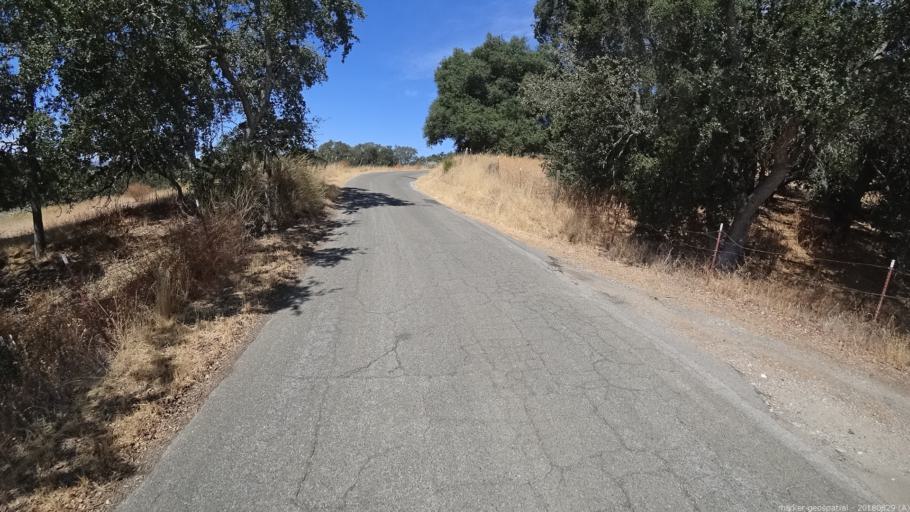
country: US
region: California
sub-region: San Luis Obispo County
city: Lake Nacimiento
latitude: 35.8063
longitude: -121.0370
